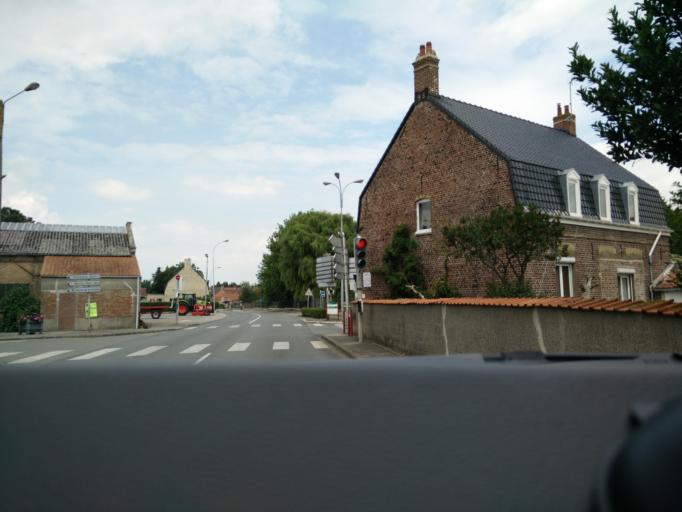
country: FR
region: Nord-Pas-de-Calais
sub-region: Departement du Nord
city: Hondschoote
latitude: 50.9765
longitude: 2.5810
